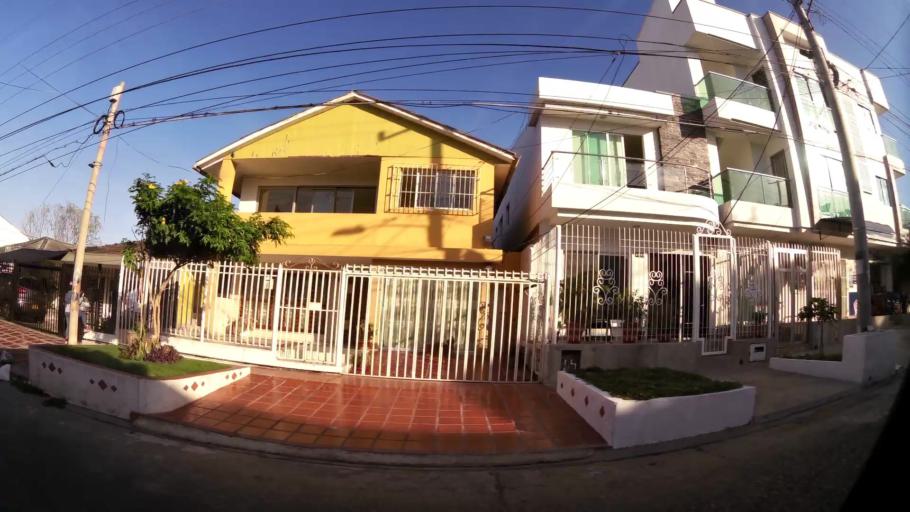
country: CO
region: Atlantico
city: Barranquilla
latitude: 10.9875
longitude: -74.8065
